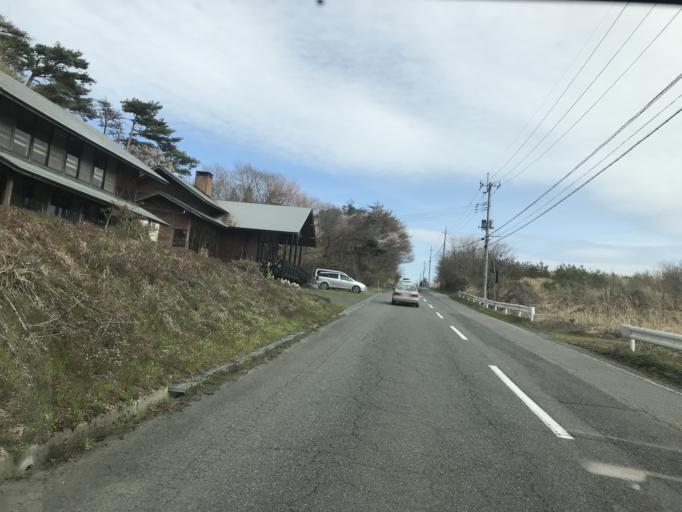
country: JP
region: Iwate
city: Ichinoseki
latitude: 38.8267
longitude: 141.2901
